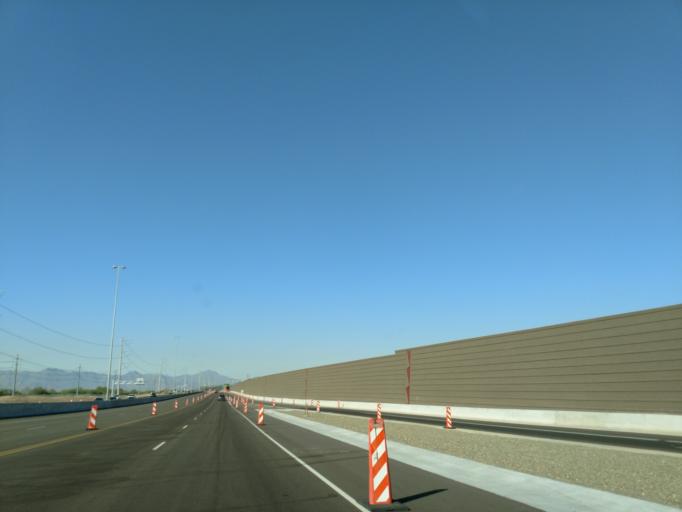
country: US
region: Arizona
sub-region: Maricopa County
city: Guadalupe
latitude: 33.2920
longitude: -112.0005
